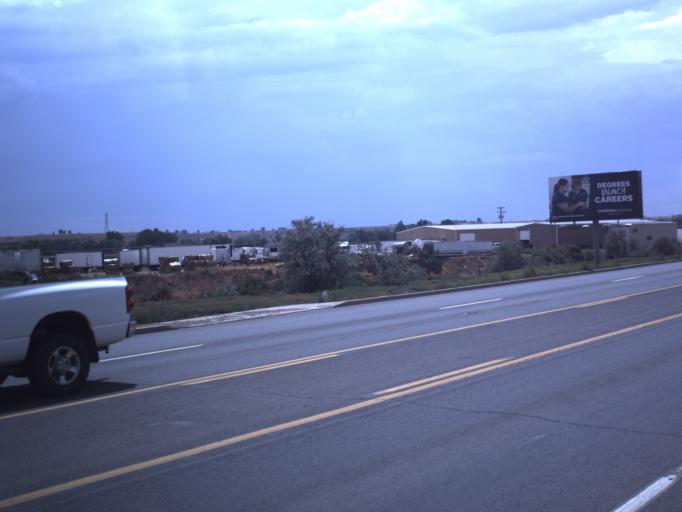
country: US
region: Utah
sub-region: Duchesne County
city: Roosevelt
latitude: 40.2846
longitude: -110.0089
